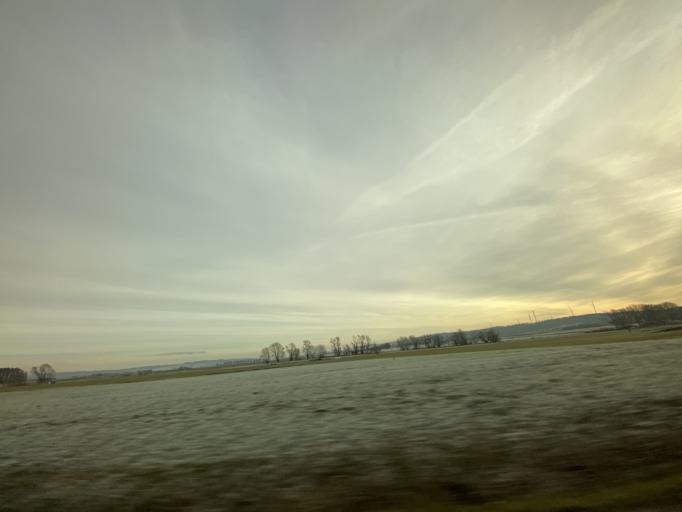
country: DE
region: Hesse
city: Amoneburg
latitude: 50.7809
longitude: 8.9039
